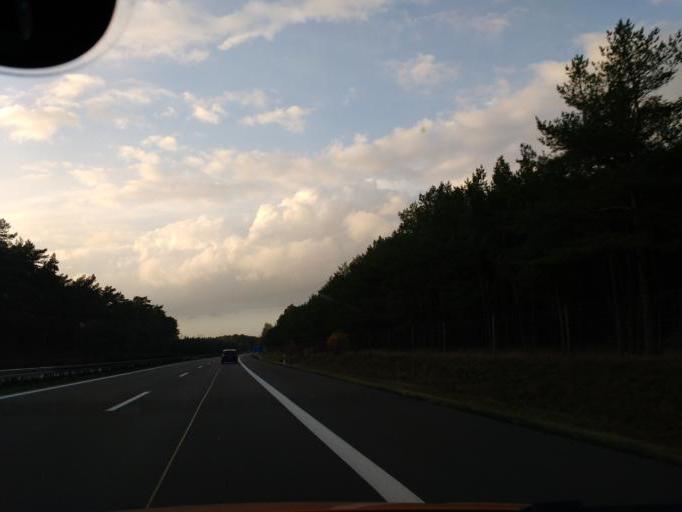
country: DE
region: Mecklenburg-Vorpommern
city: Neustadt-Glewe
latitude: 53.3728
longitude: 11.6414
